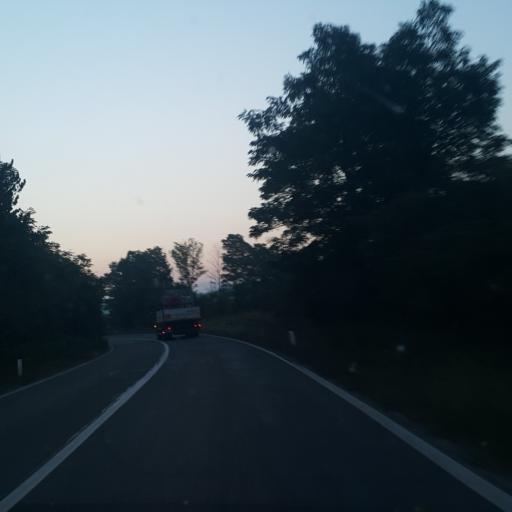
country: RS
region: Central Serbia
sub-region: Nisavski Okrug
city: Svrljig
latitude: 43.4289
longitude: 22.1462
